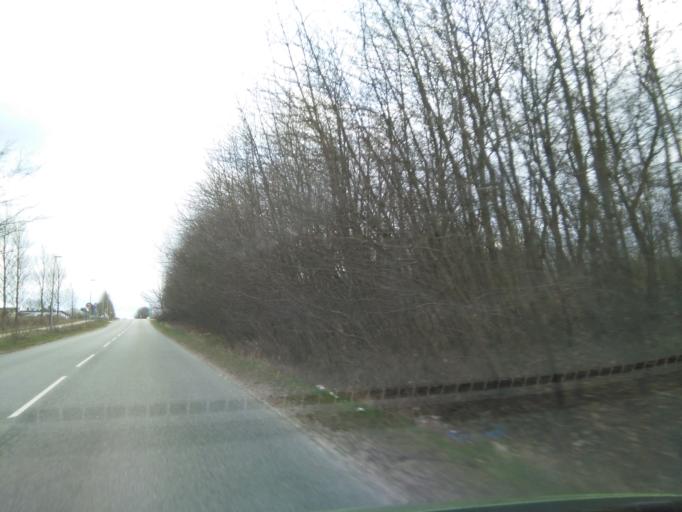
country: DK
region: Central Jutland
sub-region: Arhus Kommune
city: Stavtrup
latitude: 56.1693
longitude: 10.1196
